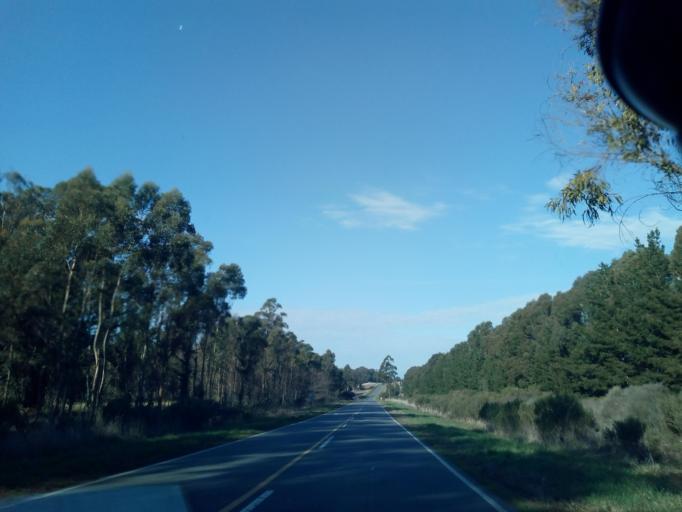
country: AR
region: Buenos Aires
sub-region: Partido de Tandil
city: Tandil
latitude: -37.3498
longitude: -58.8927
